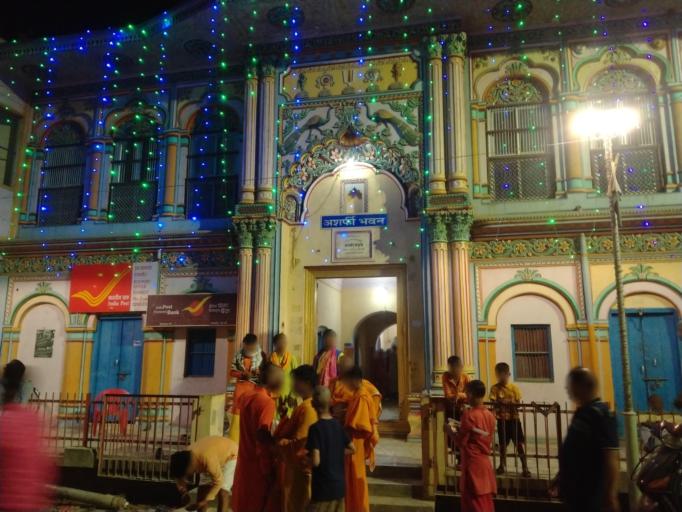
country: IN
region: Uttar Pradesh
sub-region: Faizabad
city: Ayodhya
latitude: 26.8011
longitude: 82.1969
